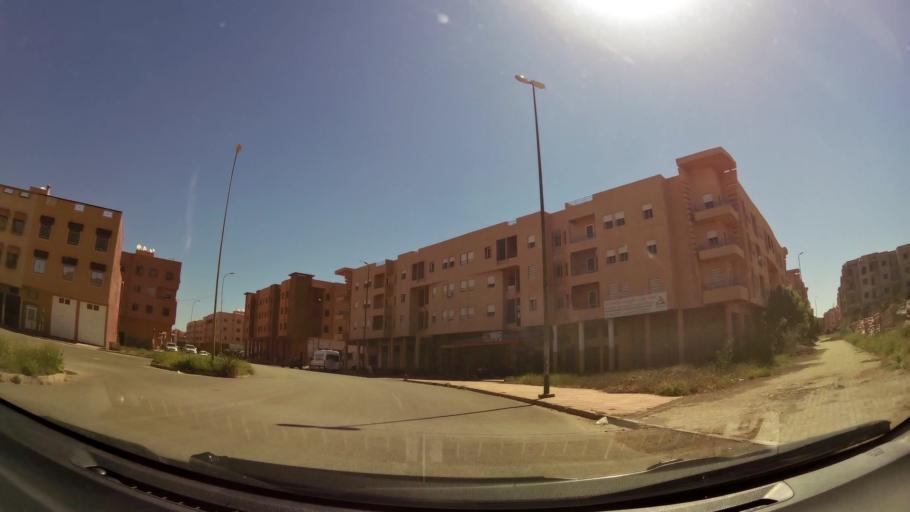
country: MA
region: Marrakech-Tensift-Al Haouz
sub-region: Marrakech
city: Marrakesh
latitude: 31.5746
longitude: -8.0597
